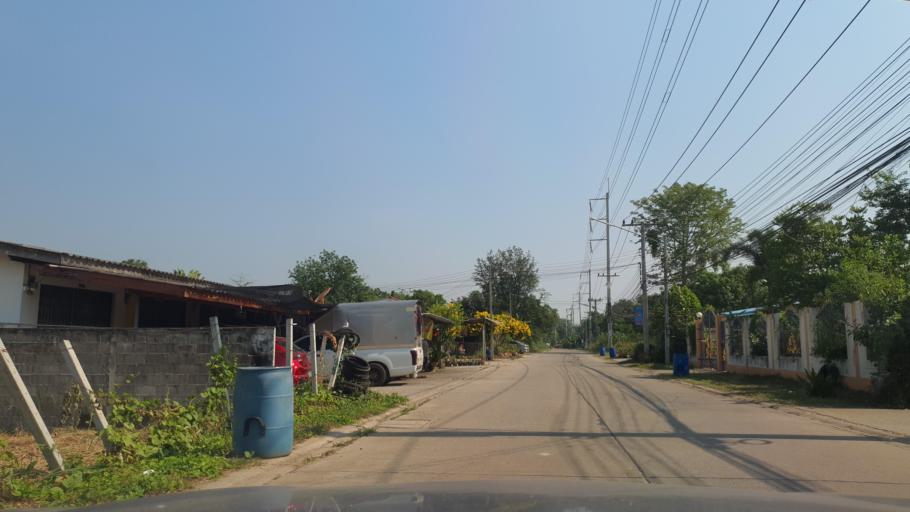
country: TH
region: Kanchanaburi
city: Kanchanaburi
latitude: 14.0641
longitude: 99.4855
